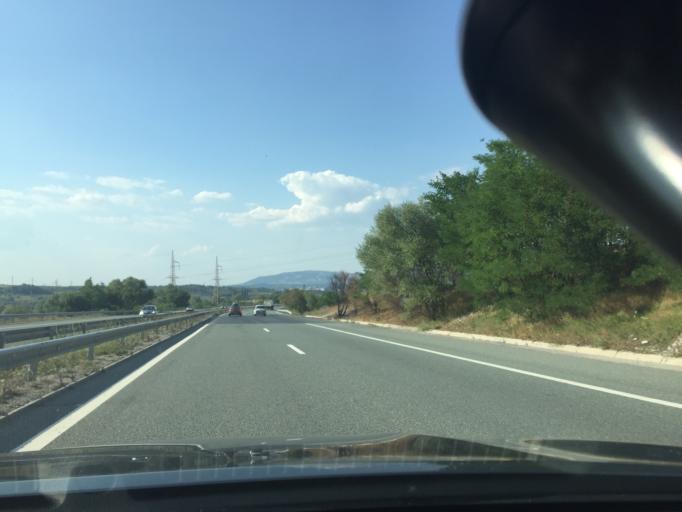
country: BG
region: Pernik
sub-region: Obshtina Pernik
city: Pernik
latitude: 42.5597
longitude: 23.1170
